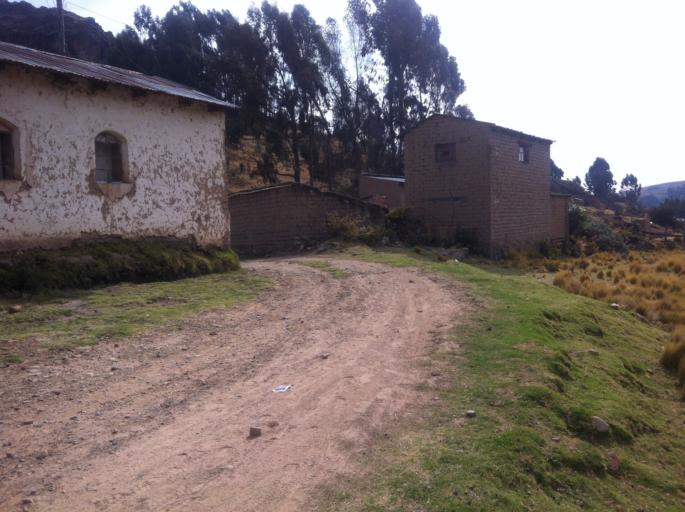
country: PE
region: Puno
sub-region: Yunguyo
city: Yunguyo
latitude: -16.1871
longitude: -69.0804
